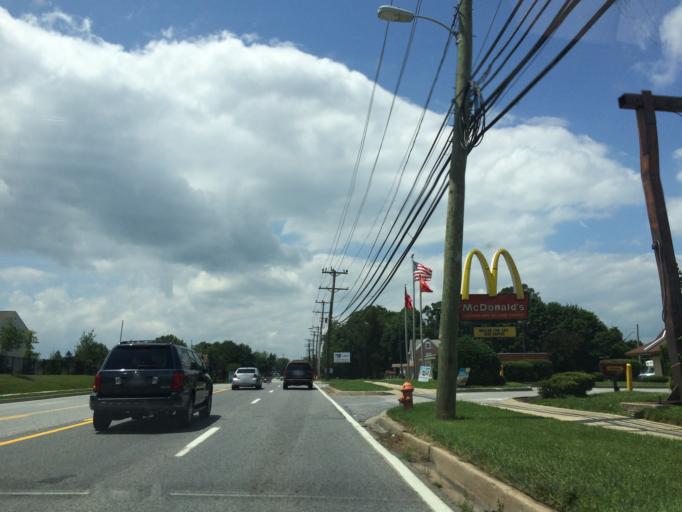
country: US
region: Maryland
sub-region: Baltimore County
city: Randallstown
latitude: 39.3744
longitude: -76.8107
